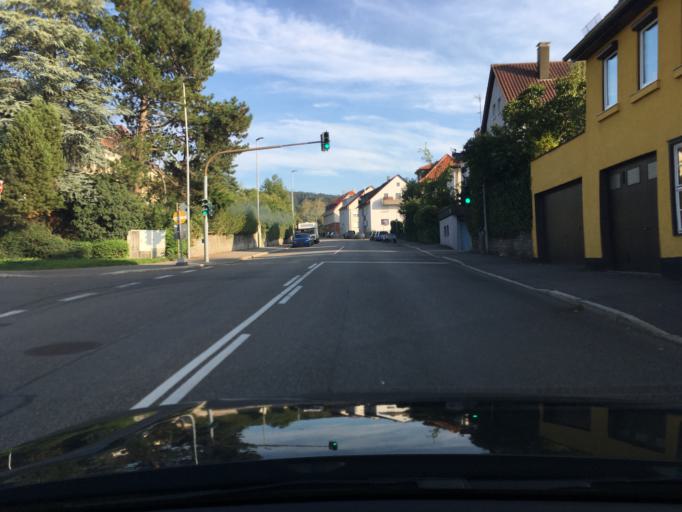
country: DE
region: Baden-Wuerttemberg
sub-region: Regierungsbezirk Stuttgart
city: Schorndorf
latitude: 48.8030
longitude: 9.5357
